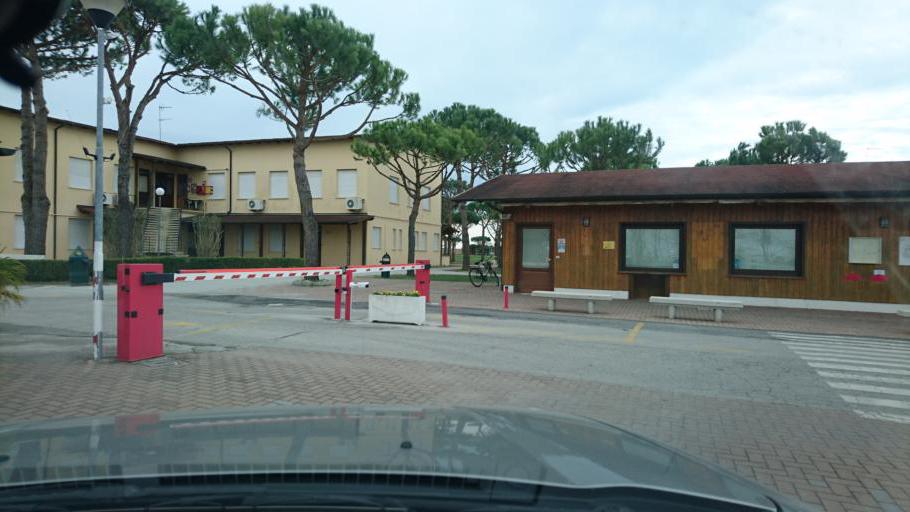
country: IT
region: Veneto
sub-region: Provincia di Venezia
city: Cavallino
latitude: 45.4585
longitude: 12.5075
